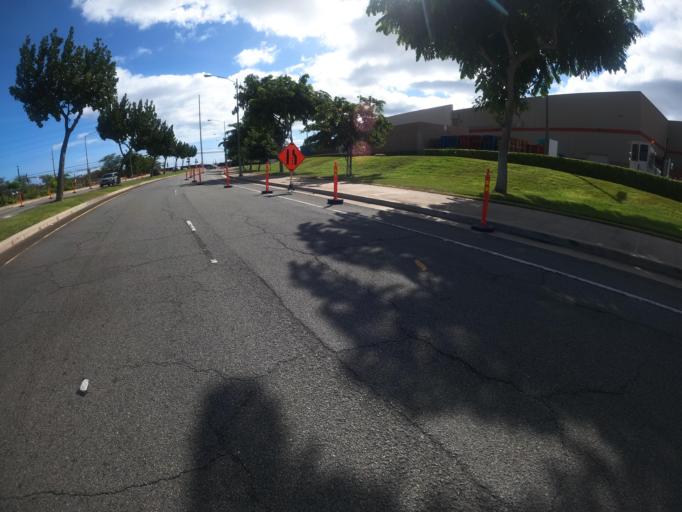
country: US
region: Hawaii
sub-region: Honolulu County
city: Makakilo City
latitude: 21.3268
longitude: -158.0864
